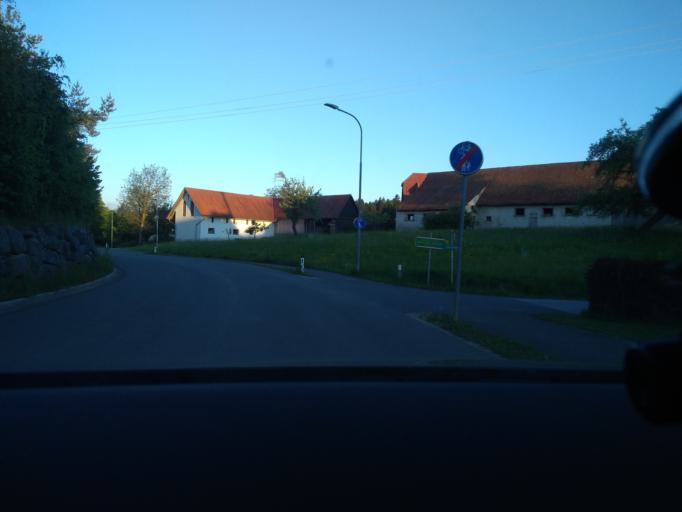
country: AT
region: Styria
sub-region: Politischer Bezirk Graz-Umgebung
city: Lieboch
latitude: 46.9625
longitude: 15.3131
